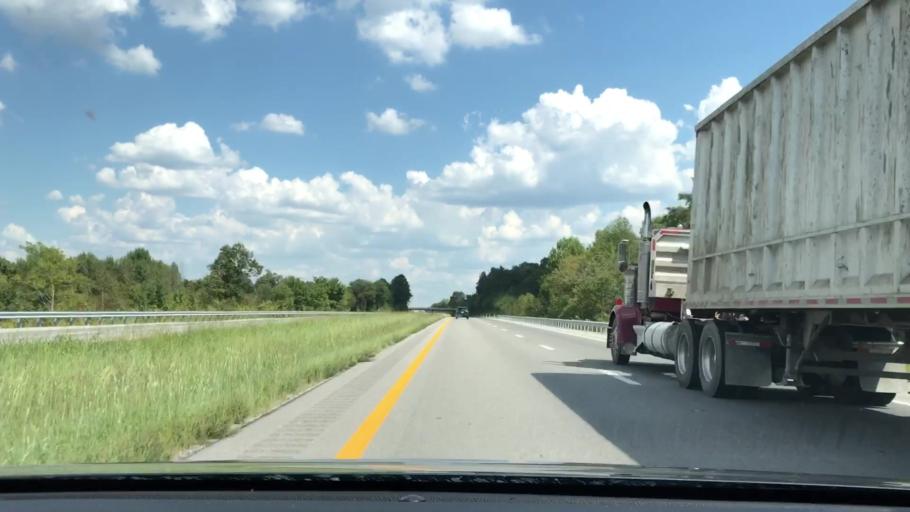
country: US
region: Kentucky
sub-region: Hopkins County
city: Dawson Springs
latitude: 37.1682
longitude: -87.7486
